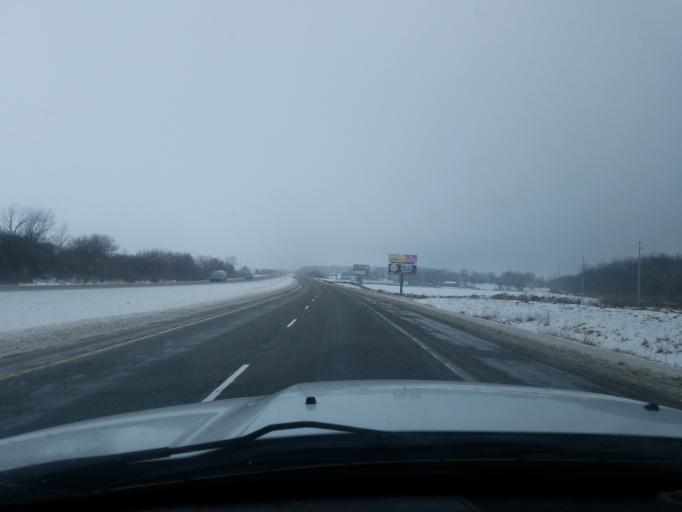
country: US
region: Indiana
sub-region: Fulton County
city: Rochester
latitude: 41.0305
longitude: -86.1836
